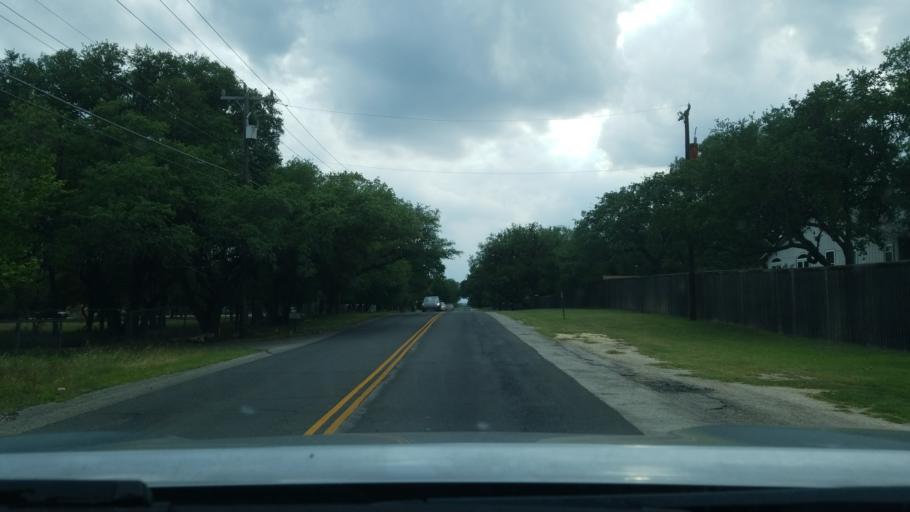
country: US
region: Texas
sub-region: Bexar County
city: Leon Valley
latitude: 29.5448
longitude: -98.5952
